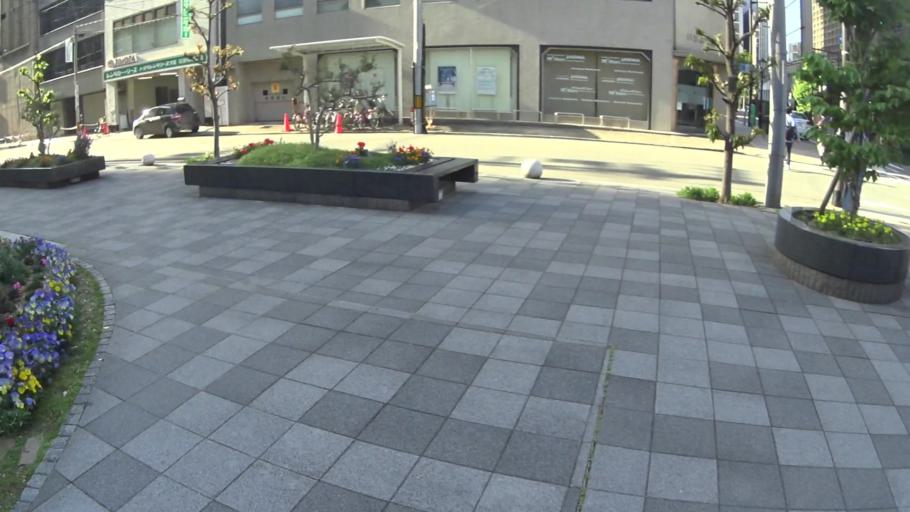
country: JP
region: Osaka
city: Osaka-shi
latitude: 34.6893
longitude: 135.5041
